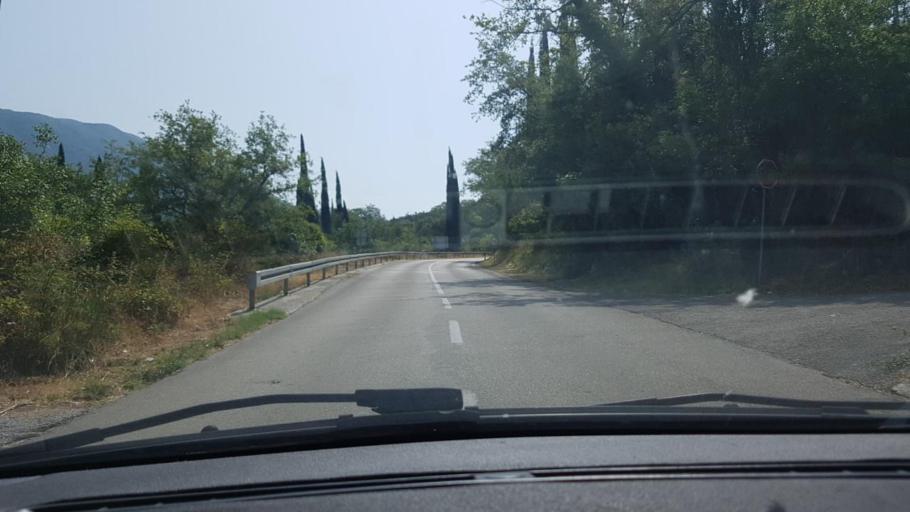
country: ME
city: Igalo
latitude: 42.5047
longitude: 18.4037
